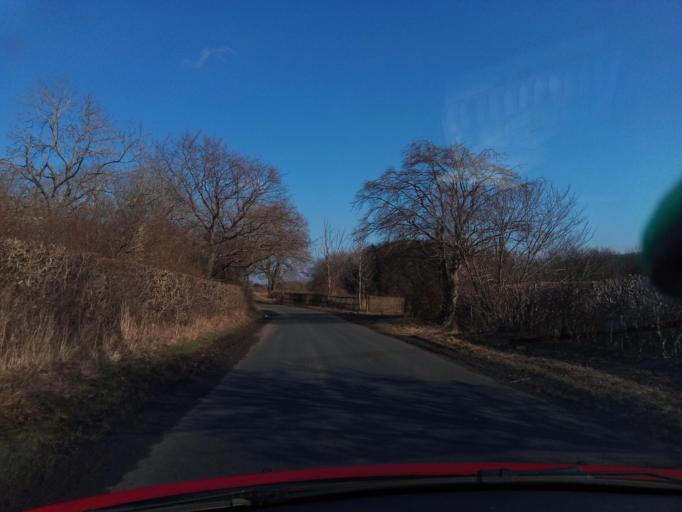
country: GB
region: Scotland
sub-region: The Scottish Borders
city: Selkirk
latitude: 55.5101
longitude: -2.7548
